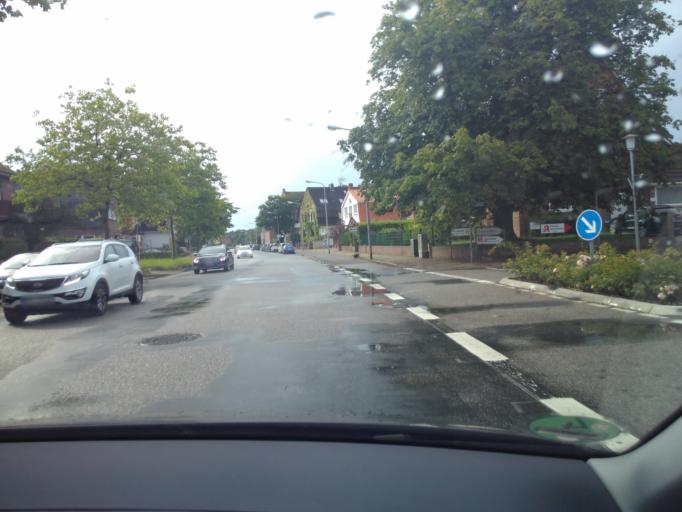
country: DE
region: Lower Saxony
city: Cuxhaven
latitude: 53.8700
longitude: 8.6916
